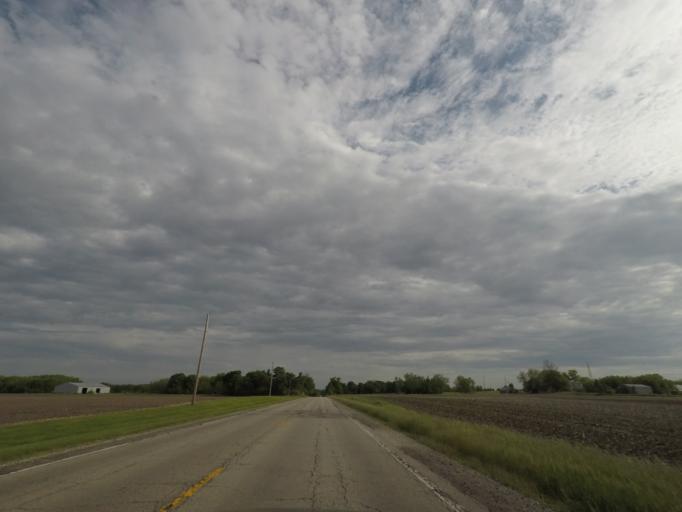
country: US
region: Illinois
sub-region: Logan County
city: Mount Pulaski
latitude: 40.0427
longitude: -89.2822
